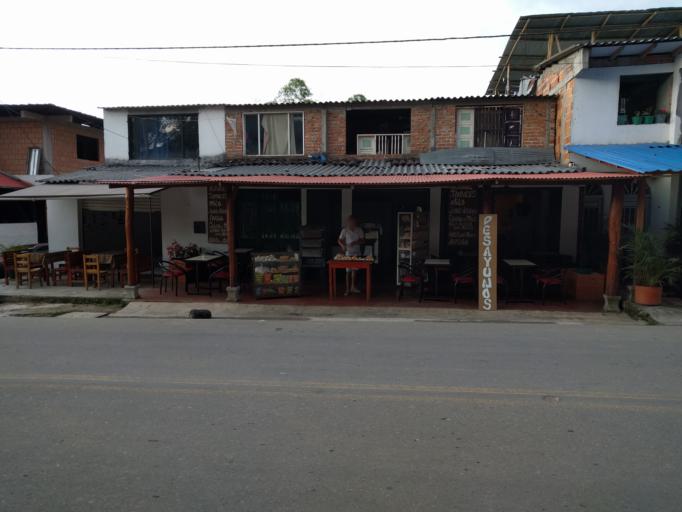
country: CO
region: Huila
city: San Agustin
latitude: 1.8864
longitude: -76.2772
